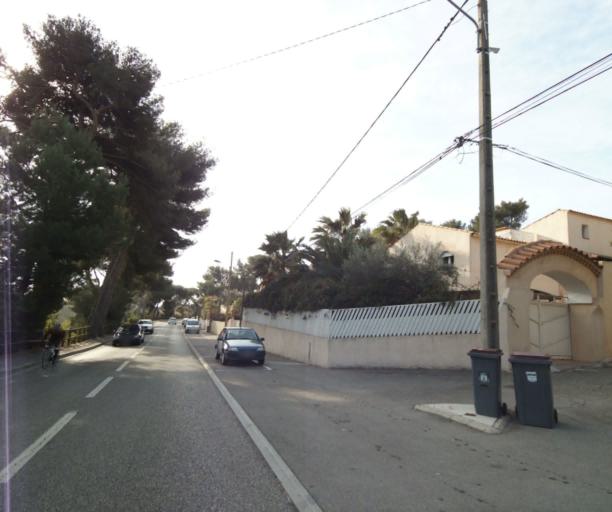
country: FR
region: Provence-Alpes-Cote d'Azur
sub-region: Departement des Bouches-du-Rhone
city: Carry-le-Rouet
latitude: 43.3323
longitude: 5.1589
